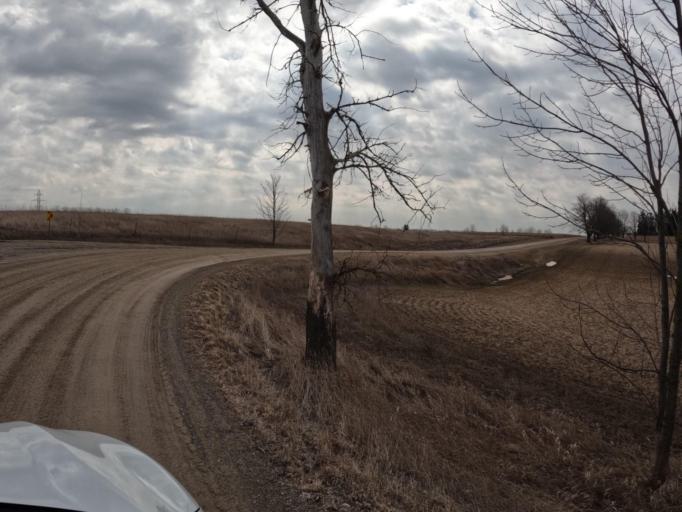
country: CA
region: Ontario
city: Shelburne
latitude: 43.9416
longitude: -80.2444
